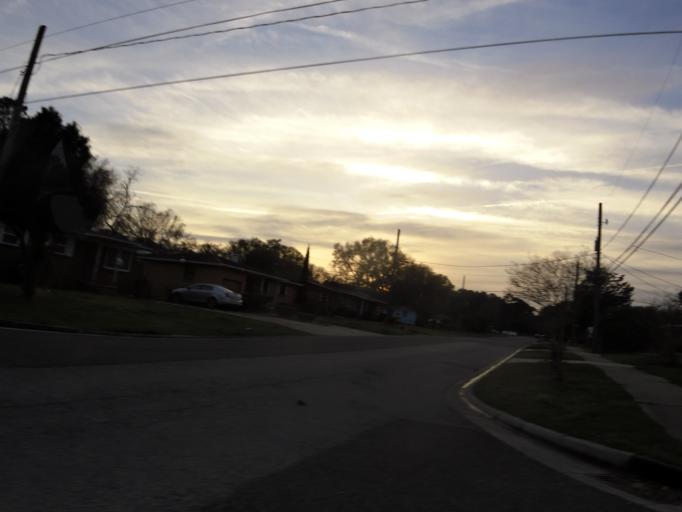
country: US
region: Florida
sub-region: Duval County
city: Jacksonville
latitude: 30.3580
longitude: -81.7051
